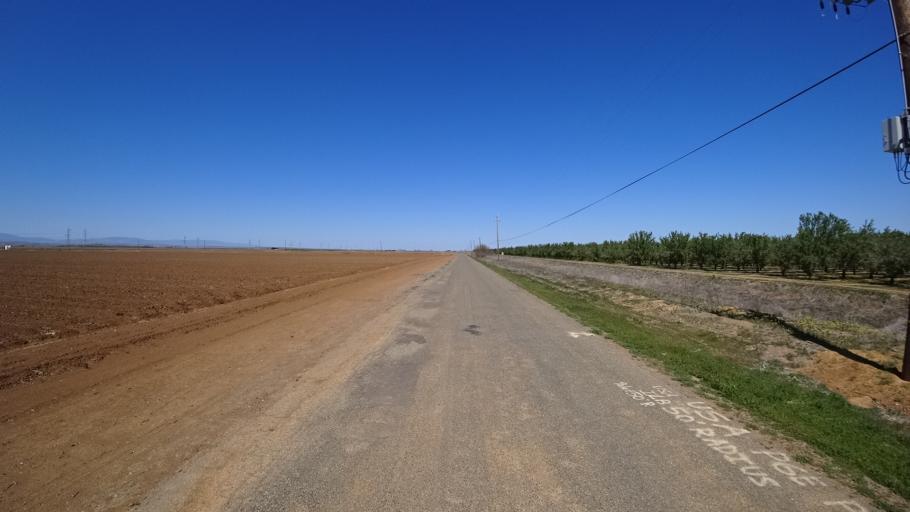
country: US
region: California
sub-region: Glenn County
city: Willows
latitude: 39.4994
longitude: -122.2773
